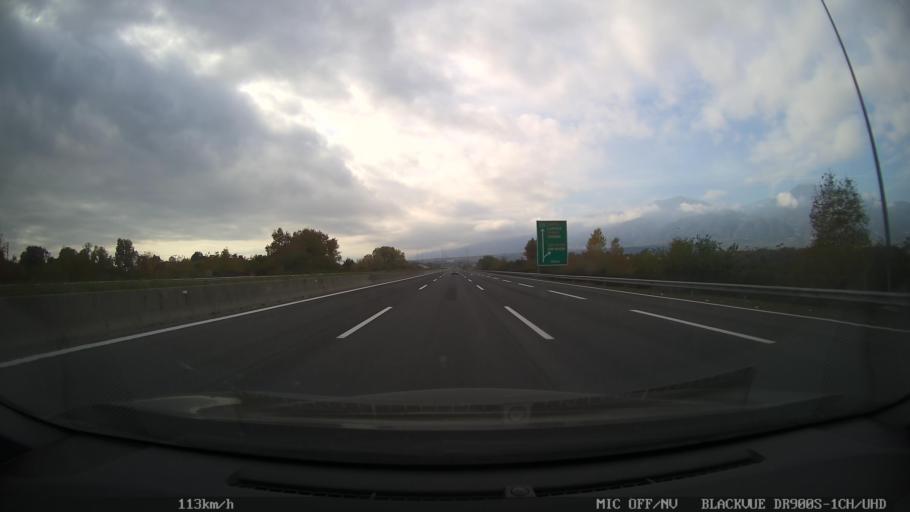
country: GR
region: Central Macedonia
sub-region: Nomos Pierias
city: Dion
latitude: 40.1579
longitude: 22.5435
